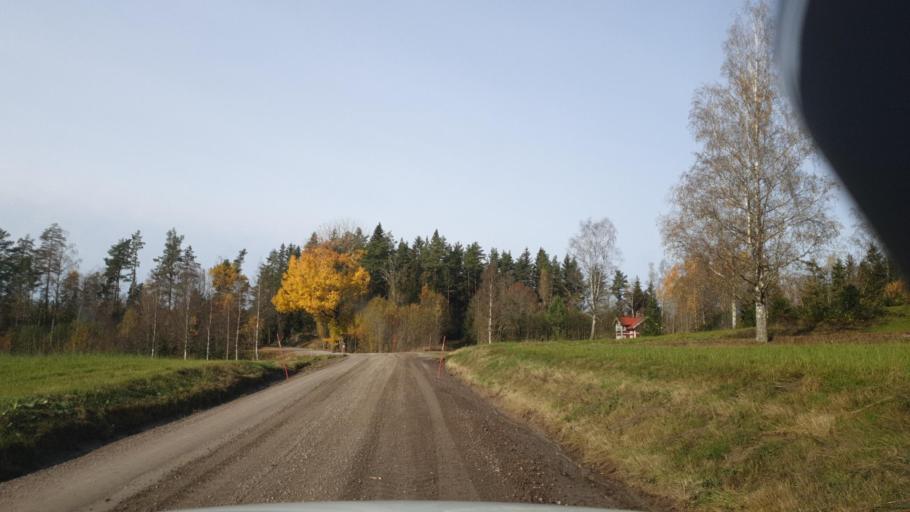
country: SE
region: Vaermland
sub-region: Eda Kommun
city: Charlottenberg
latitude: 59.7300
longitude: 12.1025
